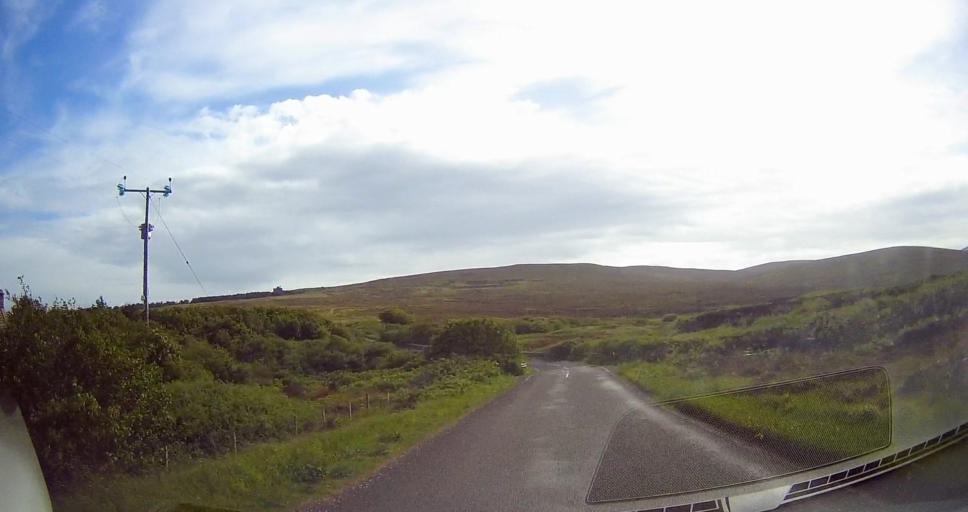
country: GB
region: Scotland
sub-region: Orkney Islands
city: Stromness
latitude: 58.8411
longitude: -3.2149
